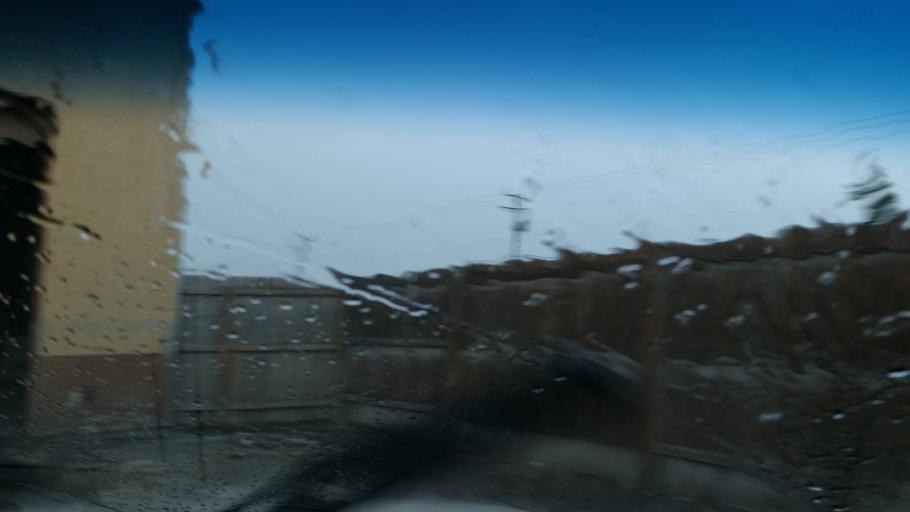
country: US
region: Indiana
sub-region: Howard County
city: Kokomo
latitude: 40.4632
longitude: -86.1225
